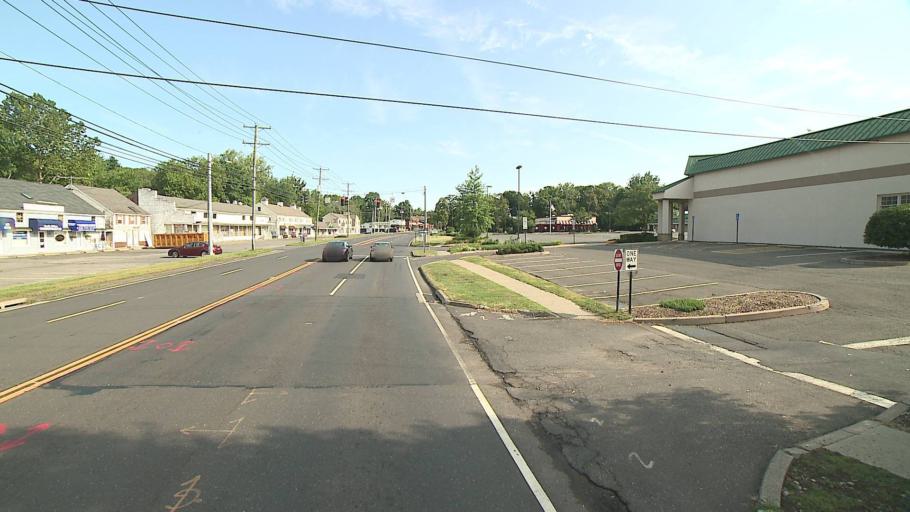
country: US
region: Connecticut
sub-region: Fairfield County
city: Wilton
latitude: 41.1612
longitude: -73.4189
